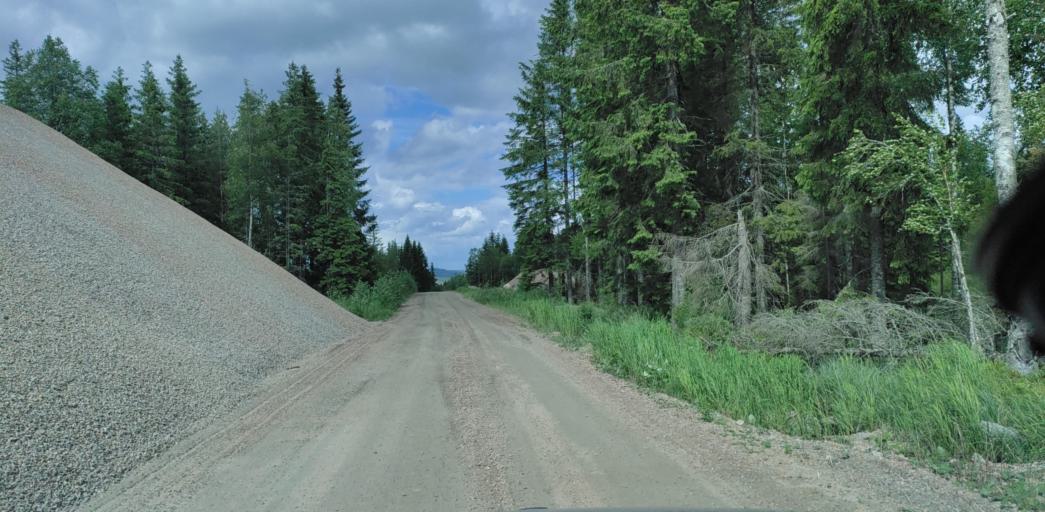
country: SE
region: Vaermland
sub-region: Munkfors Kommun
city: Munkfors
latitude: 59.9552
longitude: 13.4106
